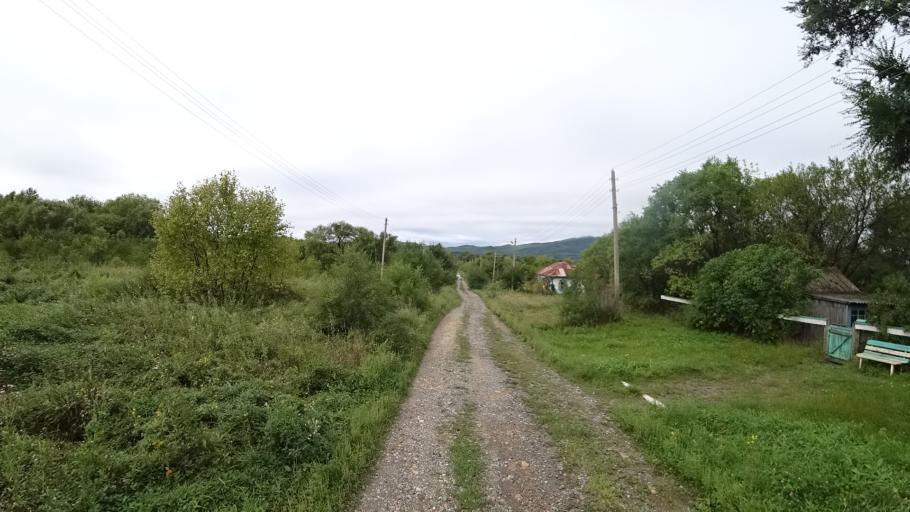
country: RU
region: Primorskiy
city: Lyalichi
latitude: 44.0769
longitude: 132.4834
